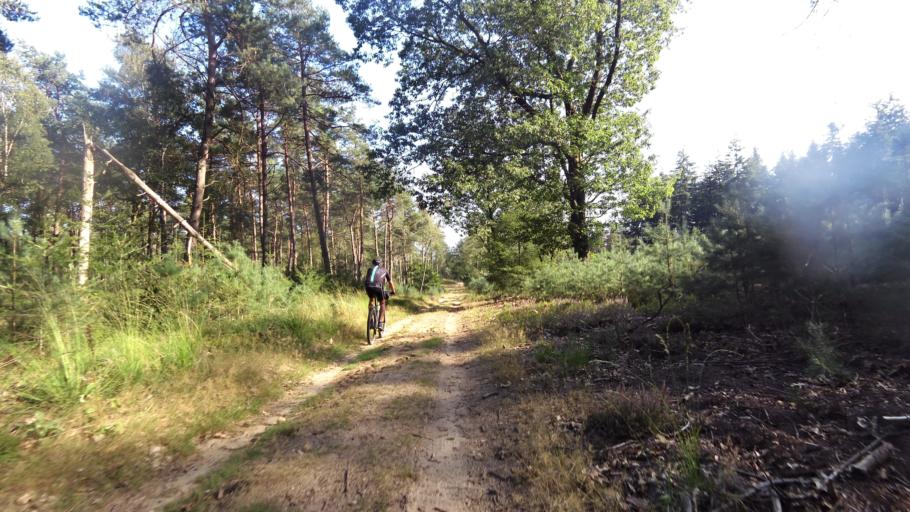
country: NL
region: Gelderland
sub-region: Gemeente Apeldoorn
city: Loenen
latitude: 52.1231
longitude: 5.9813
